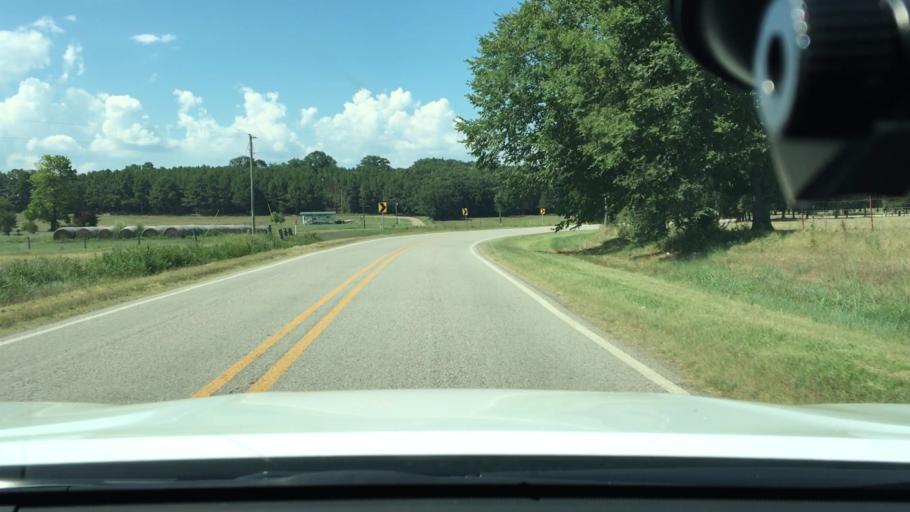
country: US
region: Arkansas
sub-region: Johnson County
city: Coal Hill
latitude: 35.3537
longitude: -93.5663
